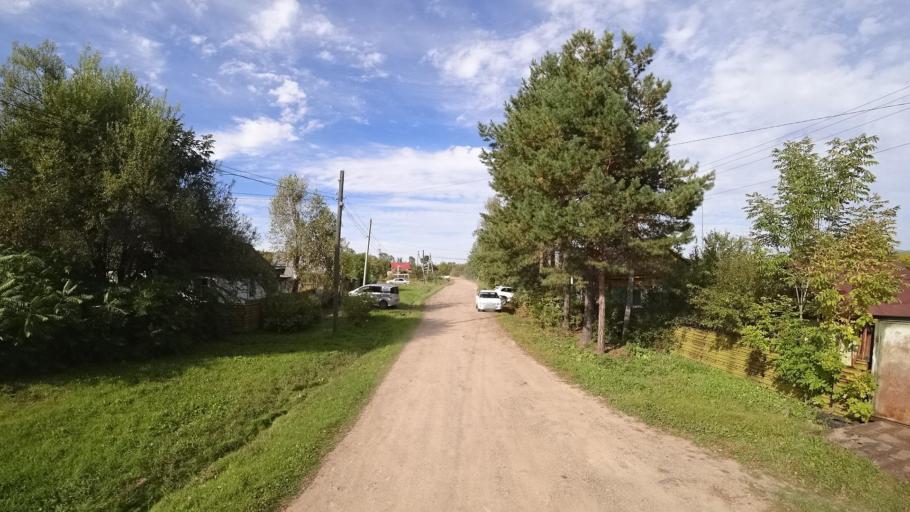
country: RU
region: Primorskiy
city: Dostoyevka
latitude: 44.2954
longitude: 133.4593
